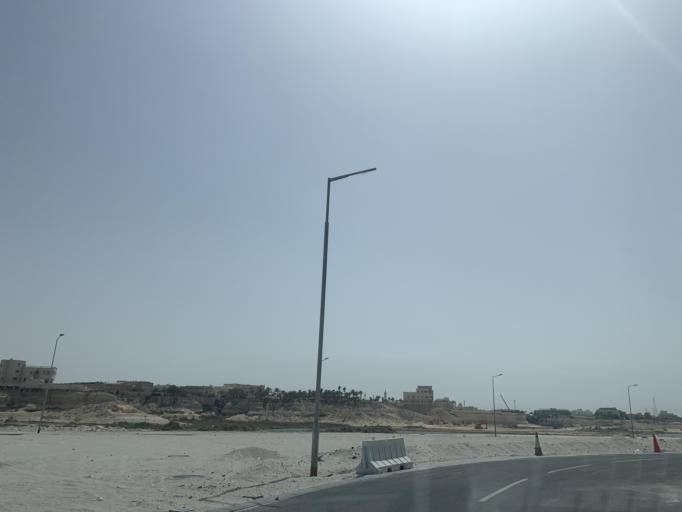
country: BH
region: Northern
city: Ar Rifa'
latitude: 26.1482
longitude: 50.5660
